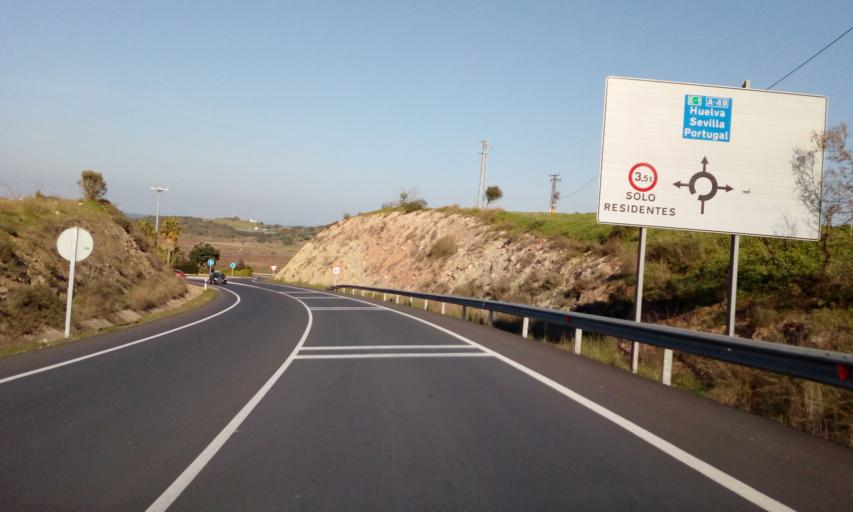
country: ES
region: Andalusia
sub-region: Provincia de Huelva
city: Ayamonte
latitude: 37.2304
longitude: -7.4010
